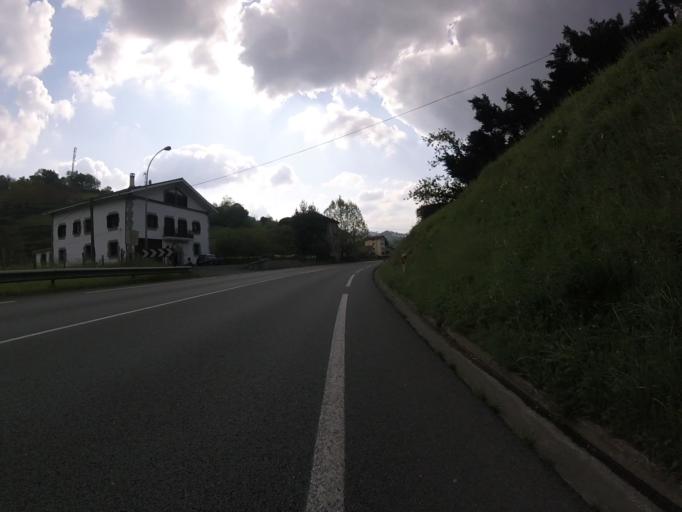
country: ES
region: Basque Country
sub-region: Provincia de Guipuzcoa
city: Azkoitia
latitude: 43.1820
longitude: -2.3205
